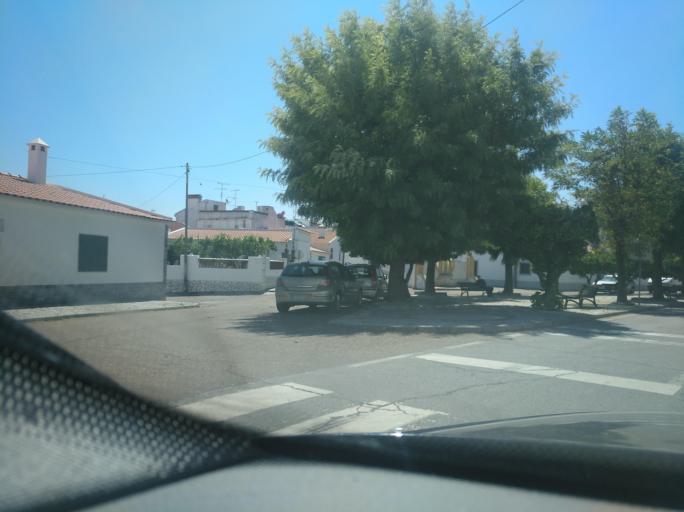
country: PT
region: Portalegre
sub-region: Elvas
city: Elvas
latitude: 38.9607
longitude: -7.2977
